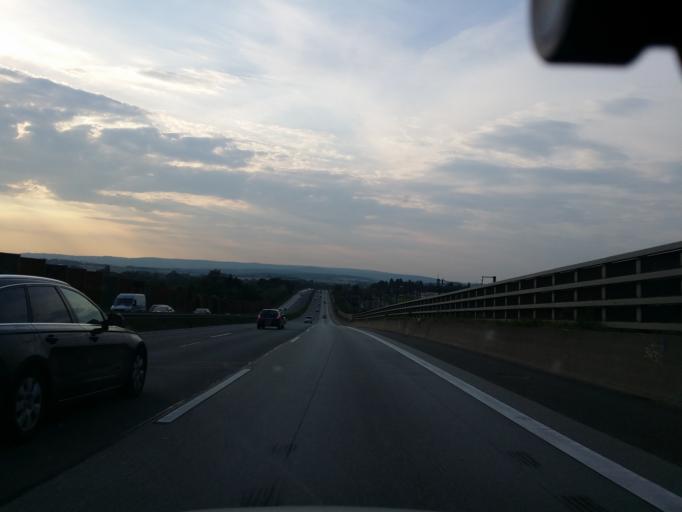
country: DE
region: Hesse
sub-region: Regierungsbezirk Darmstadt
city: Hochheim am Main
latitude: 50.0688
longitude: 8.3765
